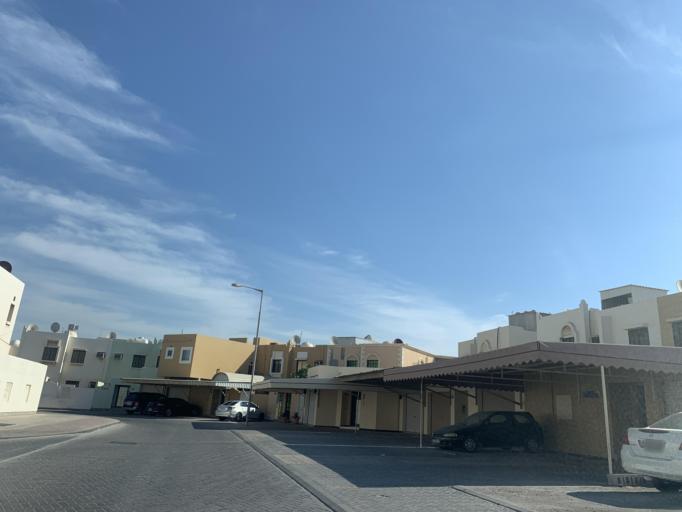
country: BH
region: Central Governorate
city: Madinat Hamad
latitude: 26.1268
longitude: 50.4967
